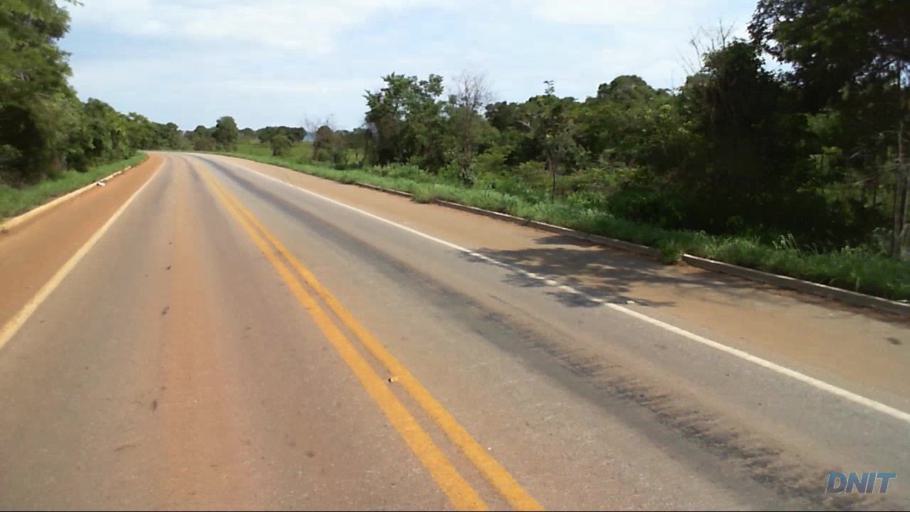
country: BR
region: Goias
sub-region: Barro Alto
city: Barro Alto
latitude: -15.0911
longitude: -48.8557
